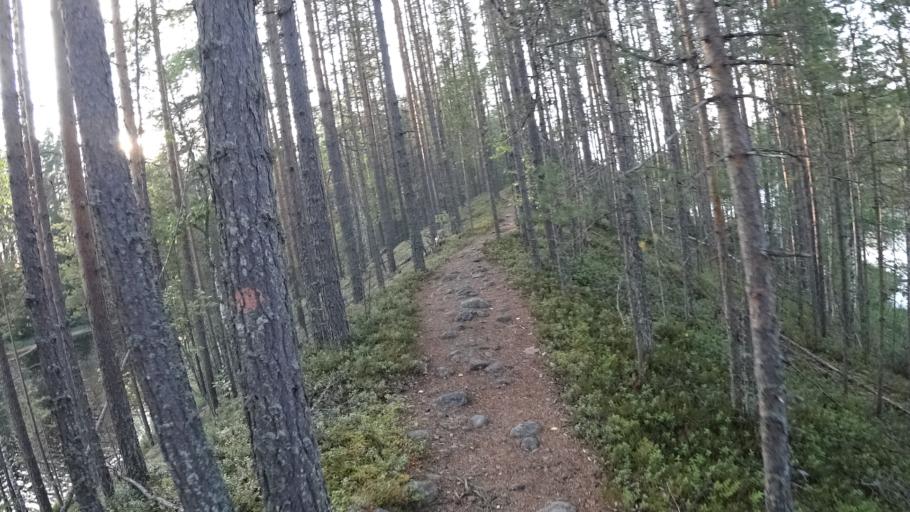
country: FI
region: North Karelia
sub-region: Joensuu
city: Ilomantsi
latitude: 62.5795
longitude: 31.1591
